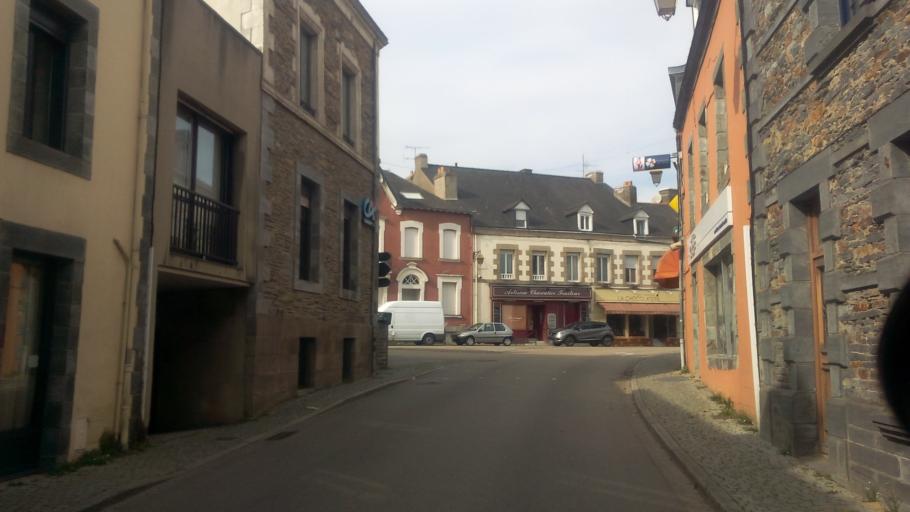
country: FR
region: Brittany
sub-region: Departement du Morbihan
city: La Gacilly
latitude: 47.7638
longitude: -2.1306
